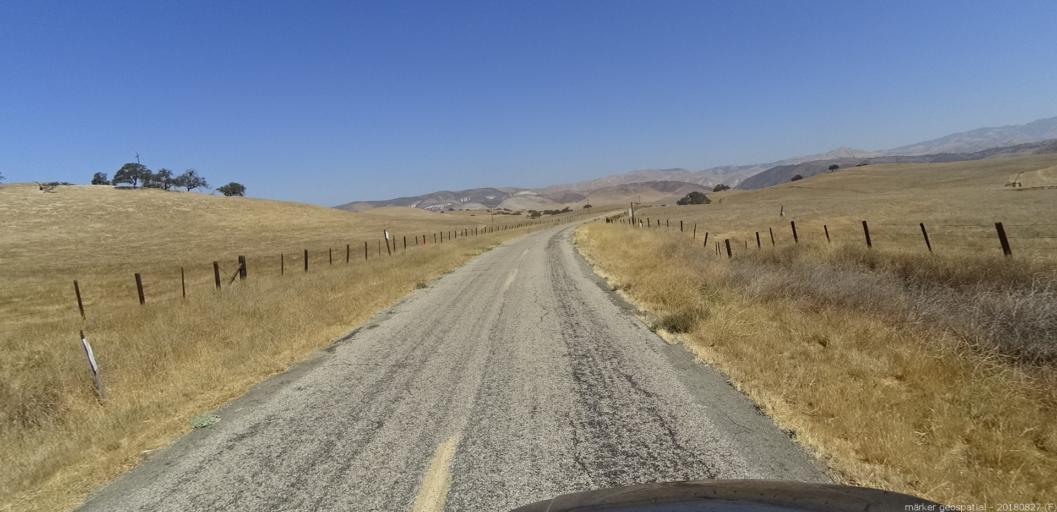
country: US
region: California
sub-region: Monterey County
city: King City
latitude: 36.2552
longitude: -120.9990
